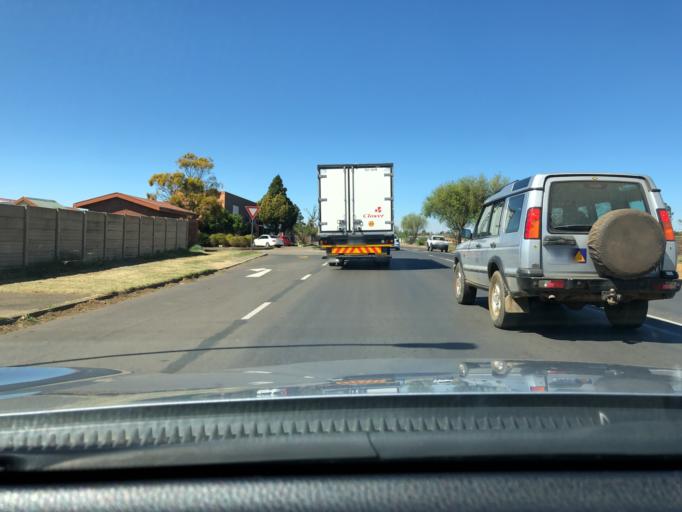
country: ZA
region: KwaZulu-Natal
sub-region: Amajuba District Municipality
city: Newcastle
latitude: -27.7585
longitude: 29.9439
